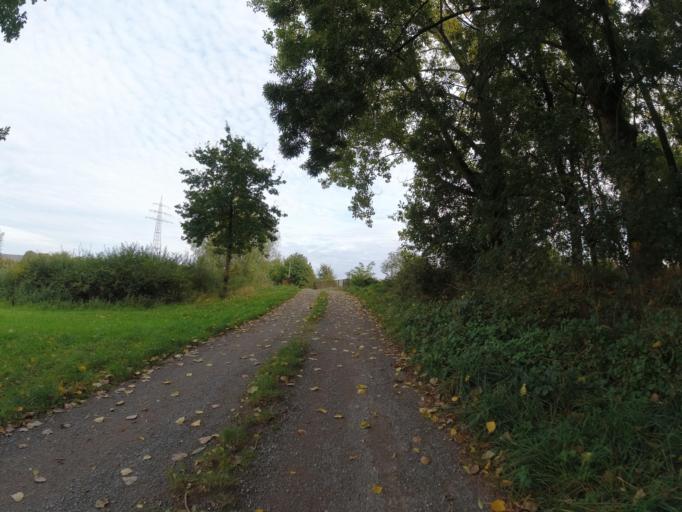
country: DE
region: North Rhine-Westphalia
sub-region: Regierungsbezirk Dusseldorf
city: Hochfeld
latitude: 51.3808
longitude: 6.7182
